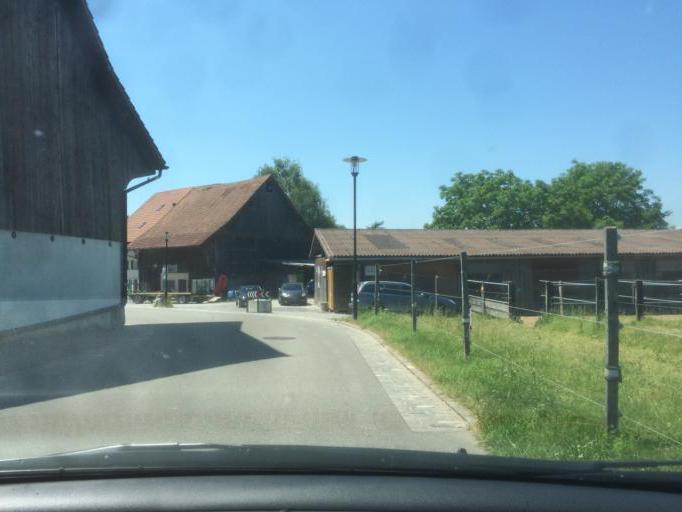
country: CH
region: Zurich
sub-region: Bezirk Uster
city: Uster / Gschwader
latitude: 47.3625
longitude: 8.7217
